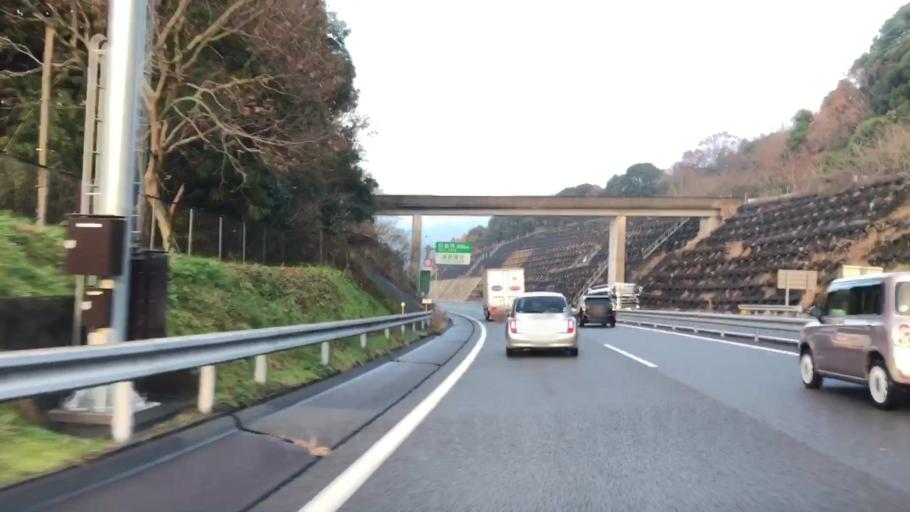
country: JP
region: Saga Prefecture
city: Imaricho-ko
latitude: 33.1685
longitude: 129.8542
